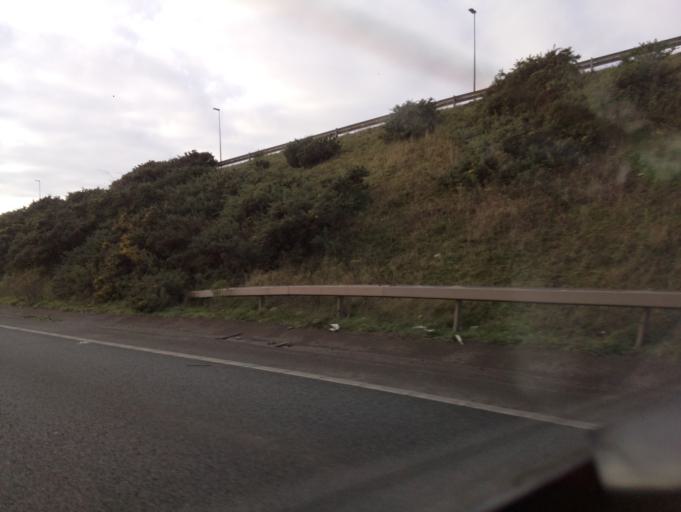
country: GB
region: England
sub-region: Staffordshire
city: Shenstone
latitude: 52.6382
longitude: -1.8038
